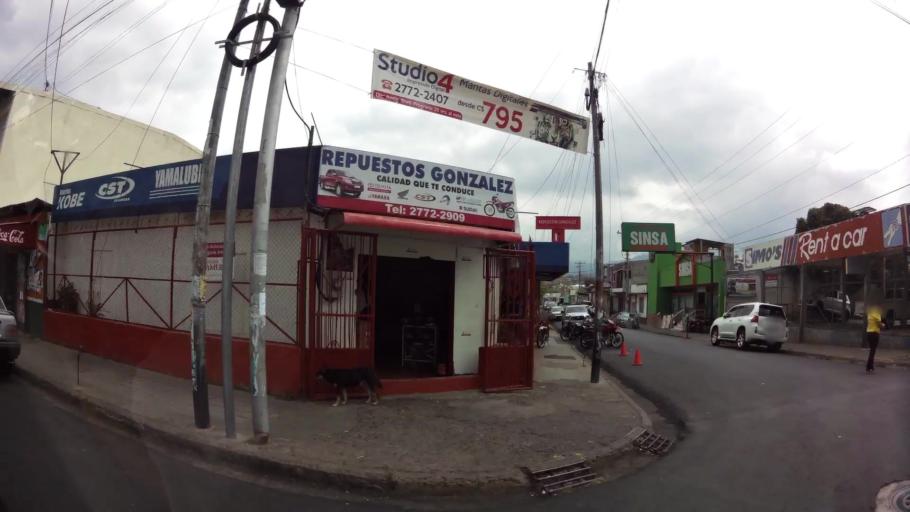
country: NI
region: Matagalpa
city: Matagalpa
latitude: 12.9217
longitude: -85.9212
